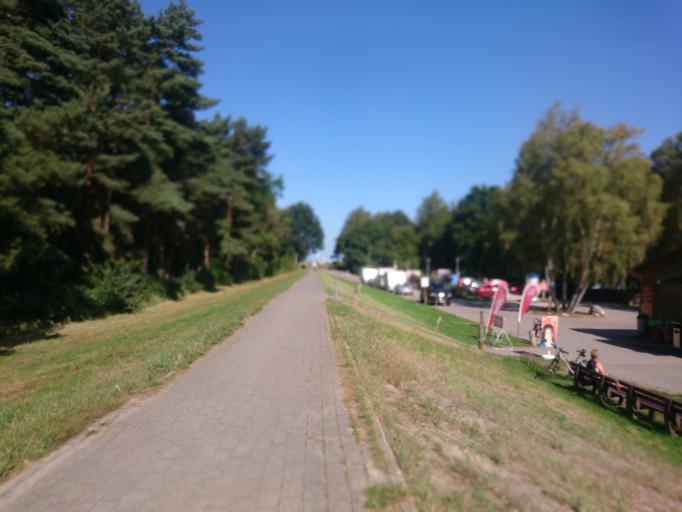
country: DE
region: Mecklenburg-Vorpommern
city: Zingst
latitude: 54.4403
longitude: 12.6600
